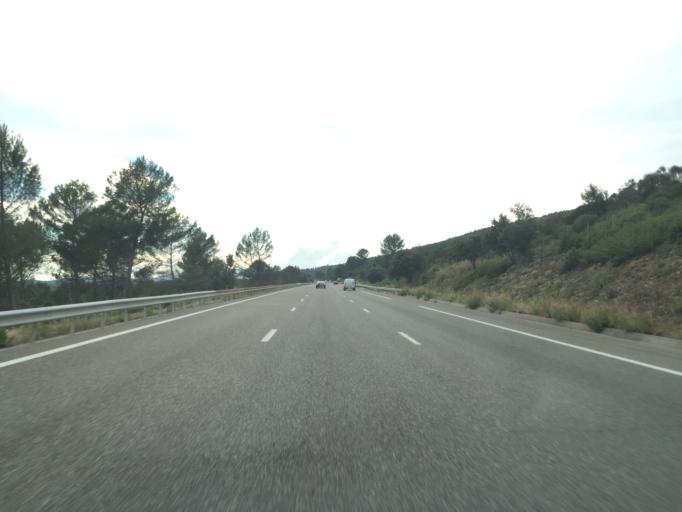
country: FR
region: Provence-Alpes-Cote d'Azur
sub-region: Departement du Var
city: La Celle
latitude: 43.4195
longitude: 6.0196
